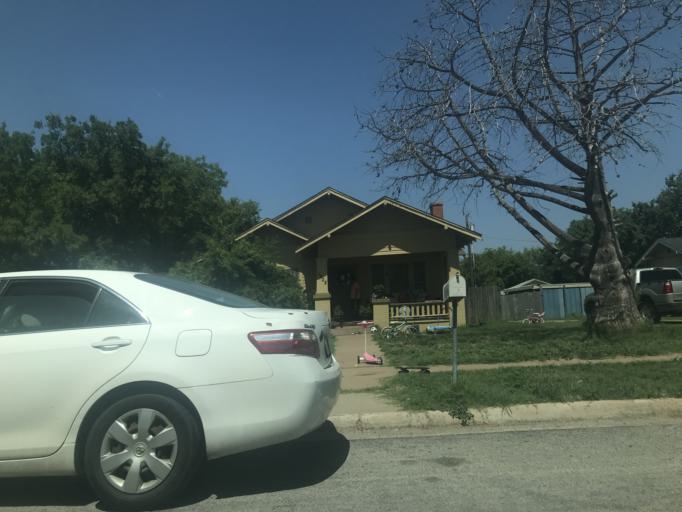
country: US
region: Texas
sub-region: Taylor County
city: Abilene
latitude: 32.4711
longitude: -99.7407
